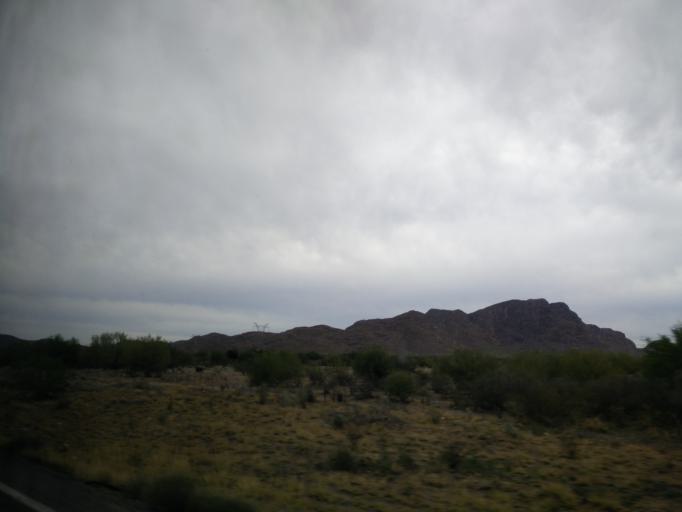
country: MX
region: Sonora
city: Hermosillo
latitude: 28.5906
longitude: -111.0245
